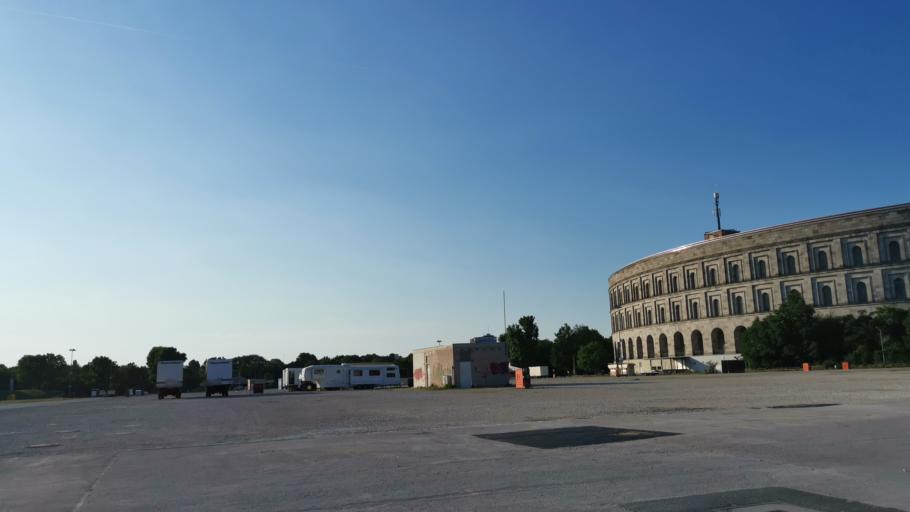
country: DE
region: Bavaria
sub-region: Regierungsbezirk Mittelfranken
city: Nuernberg
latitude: 49.4296
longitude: 11.1111
